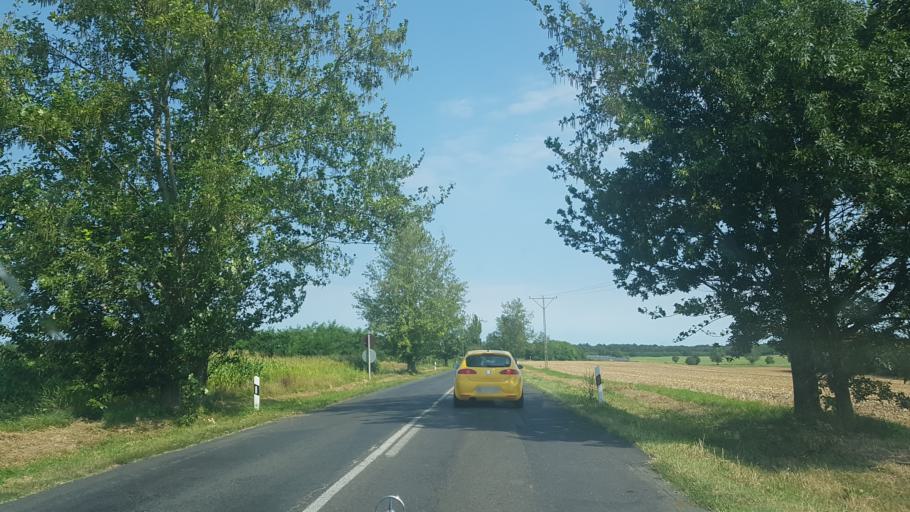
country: HU
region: Somogy
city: Bohonye
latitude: 46.4613
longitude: 17.3743
